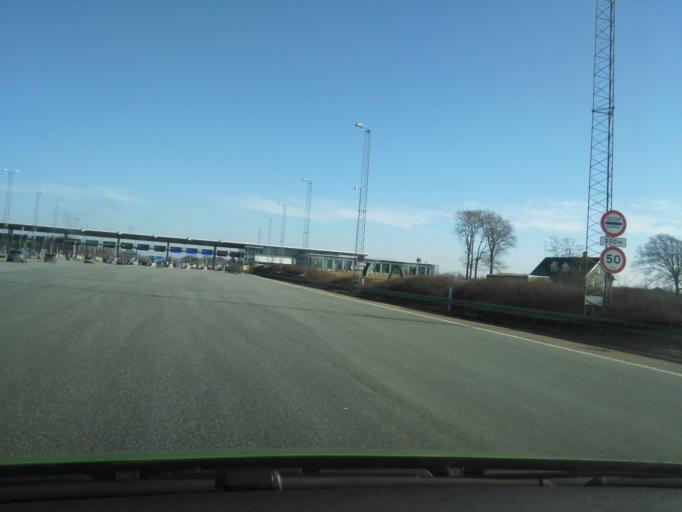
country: DK
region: Zealand
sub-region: Slagelse Kommune
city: Korsor
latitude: 55.3497
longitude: 11.1055
